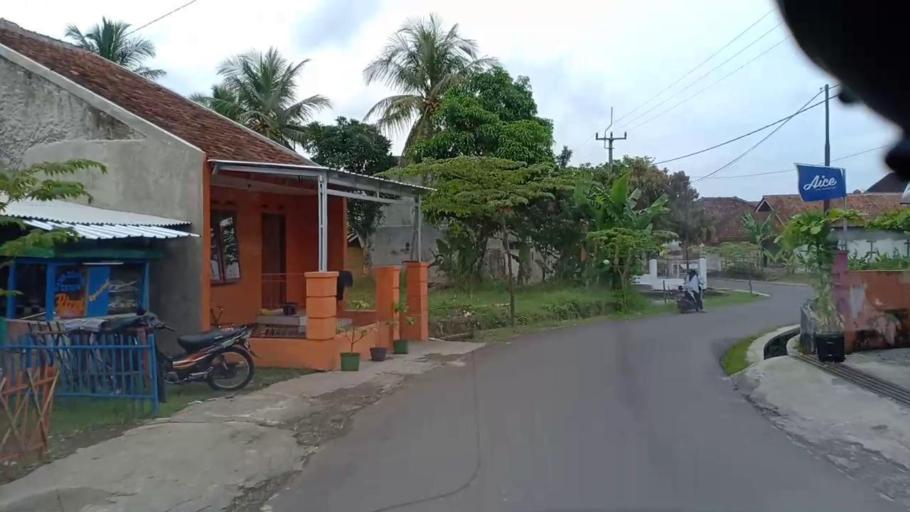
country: ID
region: West Java
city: Lemburwarung
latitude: -7.3377
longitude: 108.2710
